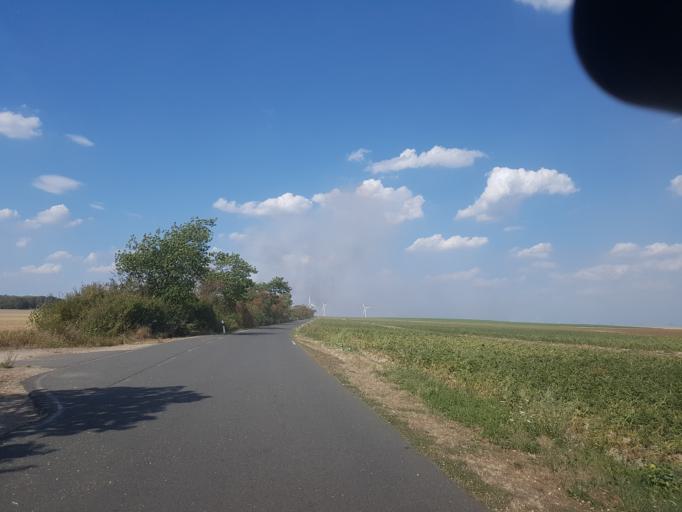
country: DE
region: Brandenburg
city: Niedergorsdorf
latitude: 51.9818
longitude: 12.8921
